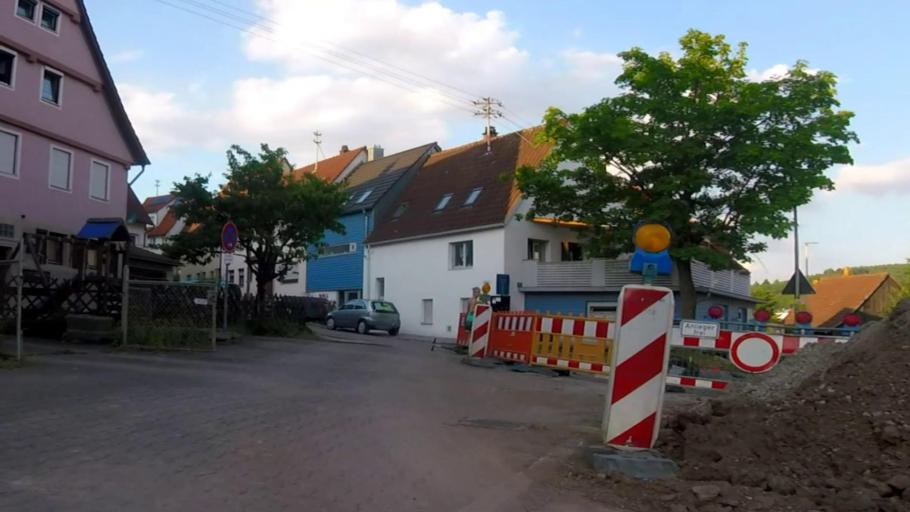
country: DE
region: Baden-Wuerttemberg
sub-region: Regierungsbezirk Stuttgart
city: Oppenweiler
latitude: 48.9898
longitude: 9.4610
